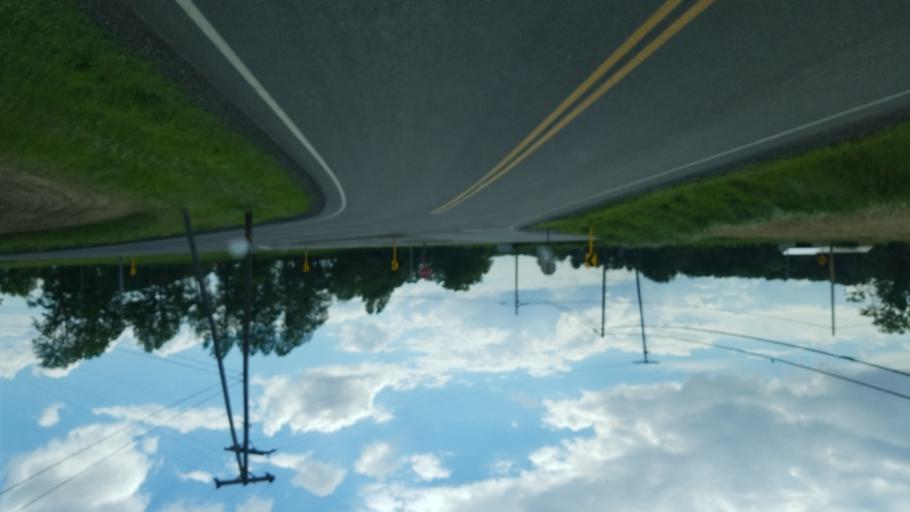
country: US
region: Ohio
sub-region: Huron County
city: Plymouth
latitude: 40.9704
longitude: -82.6202
